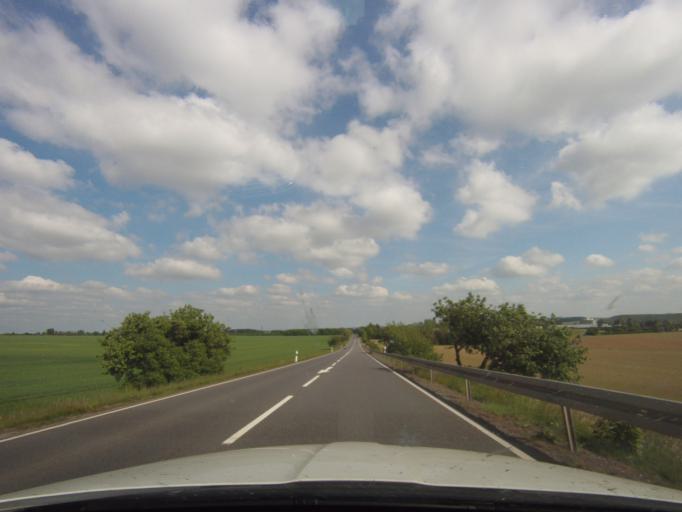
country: DE
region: Thuringia
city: Ronneburg
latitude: 50.8721
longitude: 12.1655
